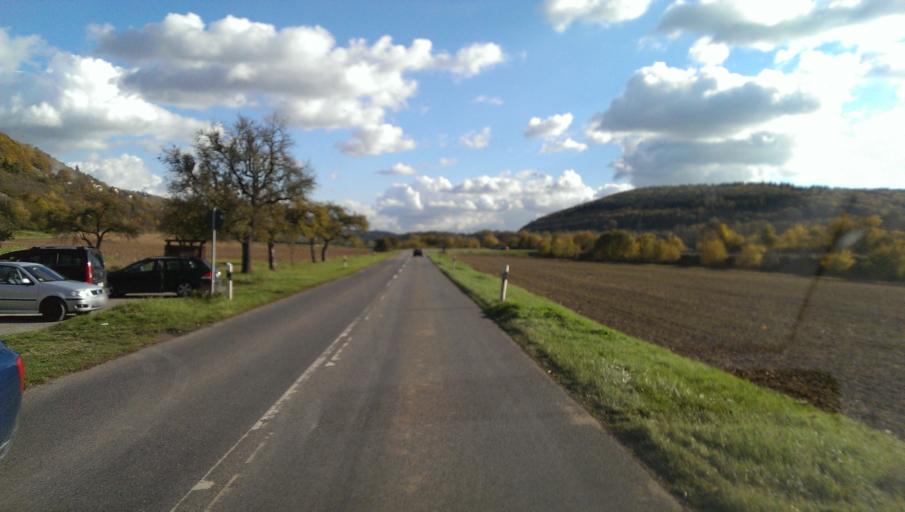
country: DE
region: Baden-Wuerttemberg
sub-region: Karlsruhe Region
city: Neckarzimmern
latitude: 49.3274
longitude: 9.1113
